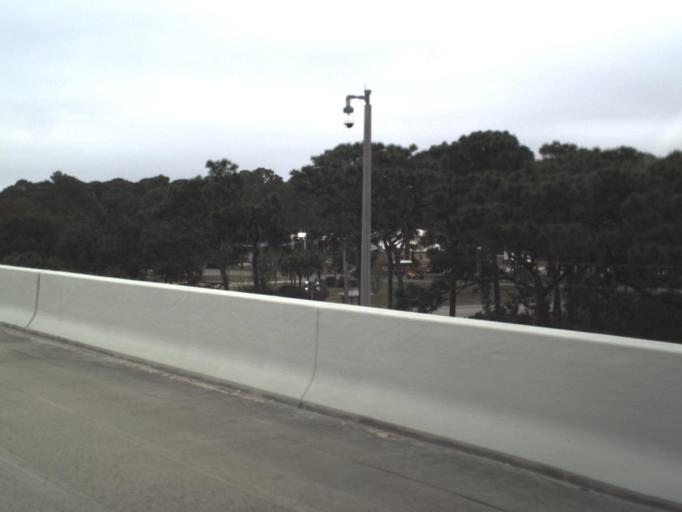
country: US
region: Florida
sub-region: Bay County
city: Upper Grand Lagoon
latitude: 30.1885
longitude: -85.7579
